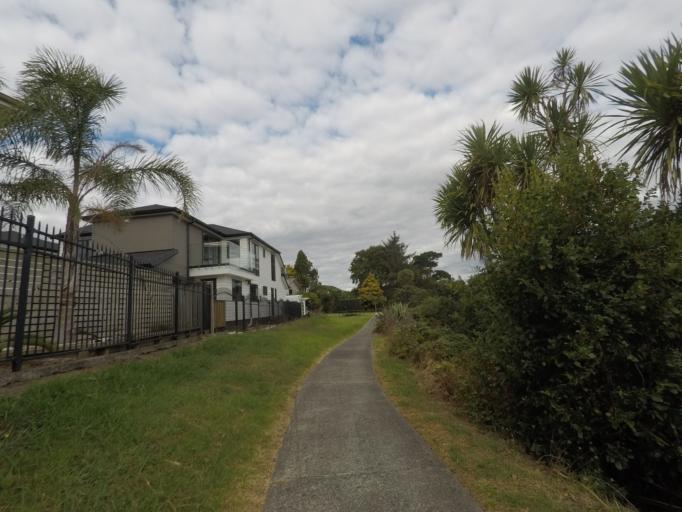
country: NZ
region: Auckland
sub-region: Auckland
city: Papakura
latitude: -37.0604
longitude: 174.9313
